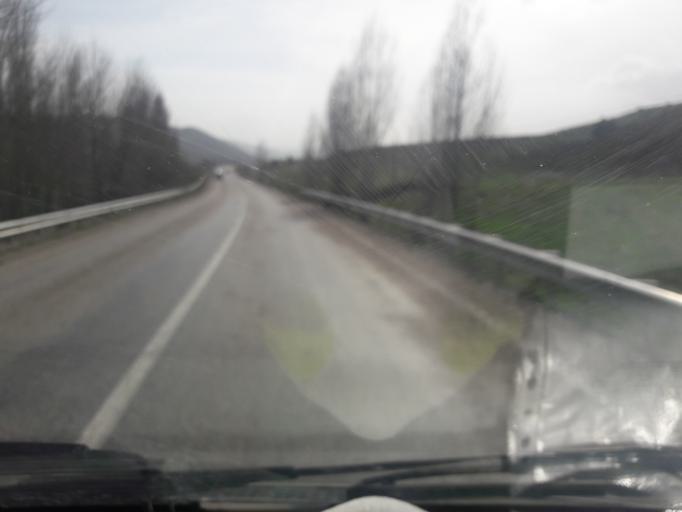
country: TR
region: Gumushane
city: Kelkit
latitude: 40.1288
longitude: 39.3567
